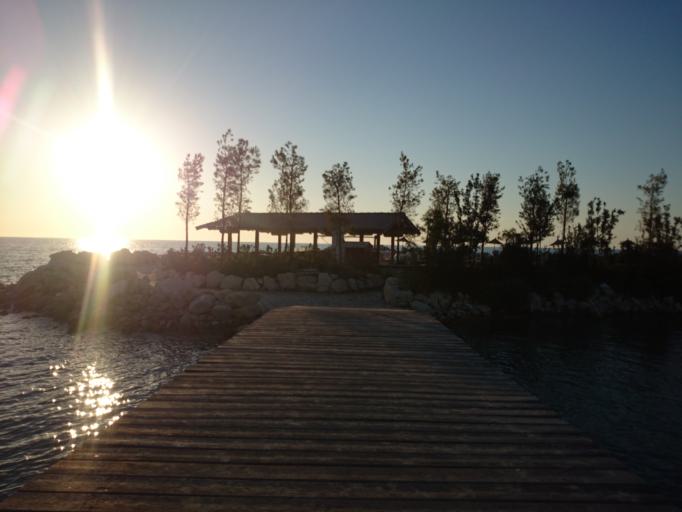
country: AL
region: Tirane
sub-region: Rrethi i Tiranes
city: Shengjergj
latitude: 41.1830
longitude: 19.4761
